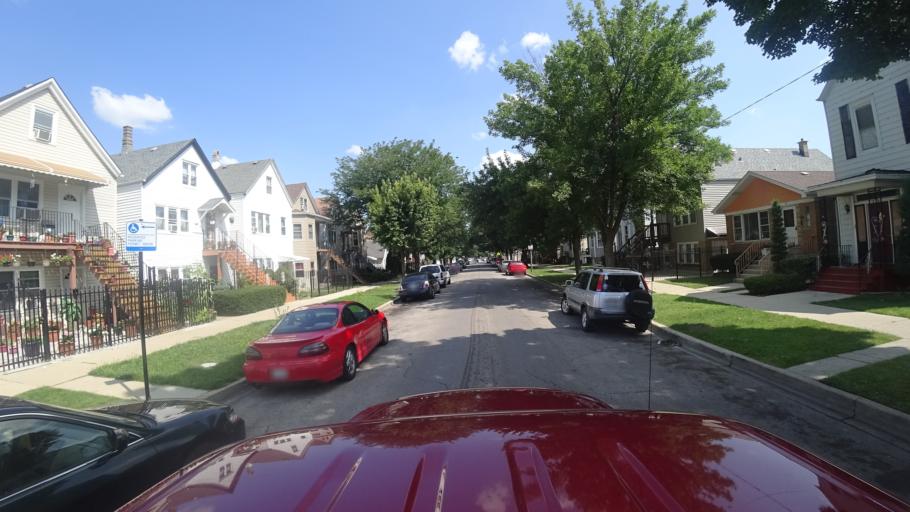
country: US
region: Illinois
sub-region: Cook County
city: Chicago
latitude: 41.7998
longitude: -87.6879
